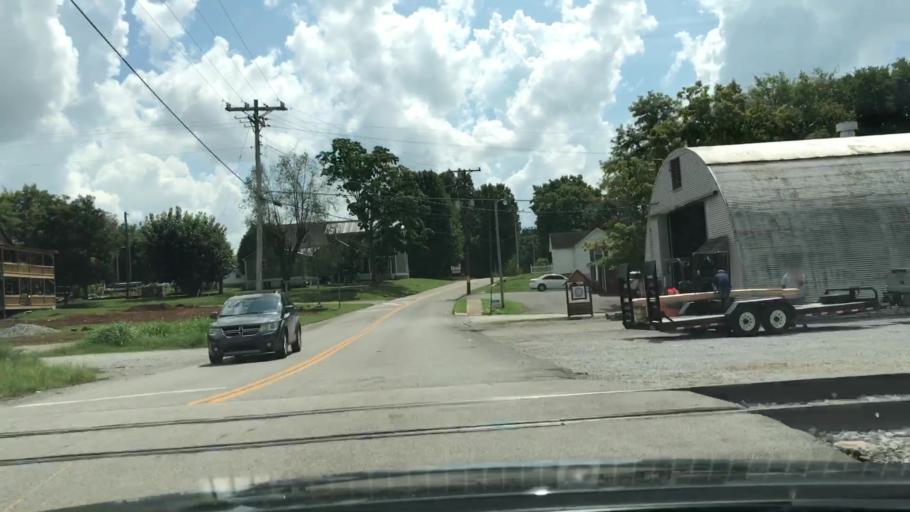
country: US
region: Kentucky
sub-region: Todd County
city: Guthrie
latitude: 36.7170
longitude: -87.0674
